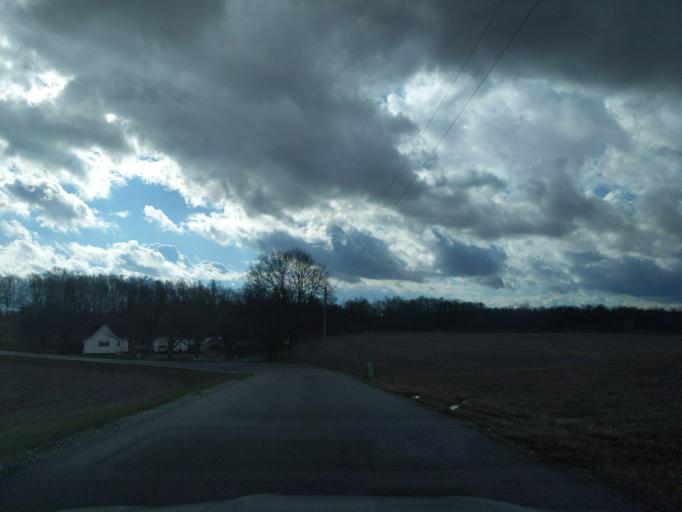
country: US
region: Indiana
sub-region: Decatur County
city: Greensburg
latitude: 39.4132
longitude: -85.5124
